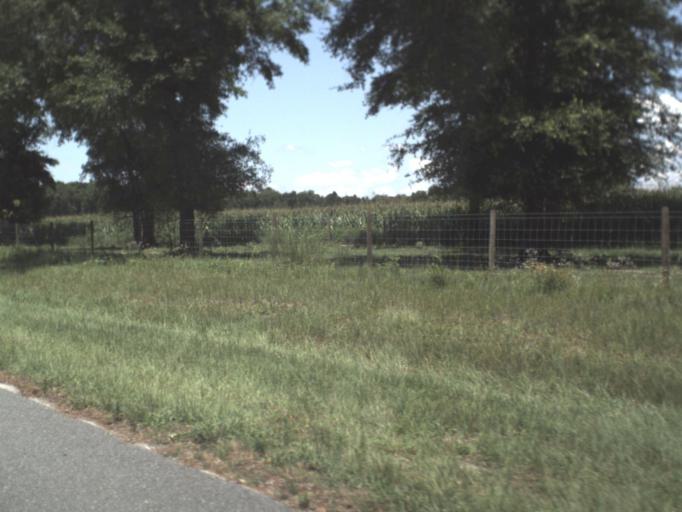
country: US
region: Florida
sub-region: Dixie County
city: Cross City
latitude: 29.8351
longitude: -82.9685
